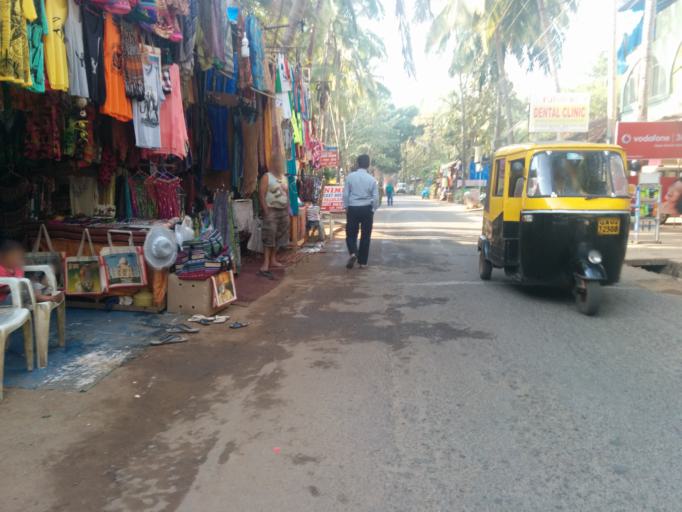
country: IN
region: Goa
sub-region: South Goa
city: Kankon
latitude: 15.0108
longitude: 74.0260
